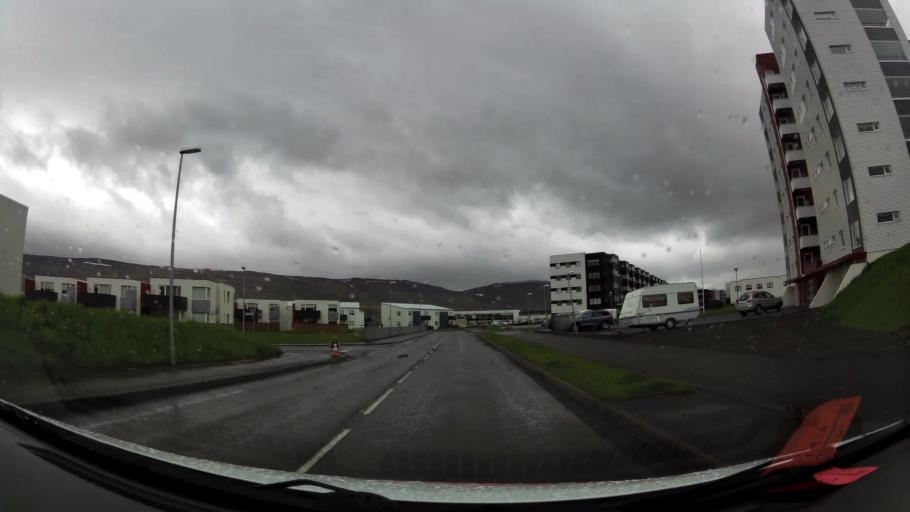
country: IS
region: Northeast
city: Akureyri
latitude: 65.6660
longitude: -18.1045
